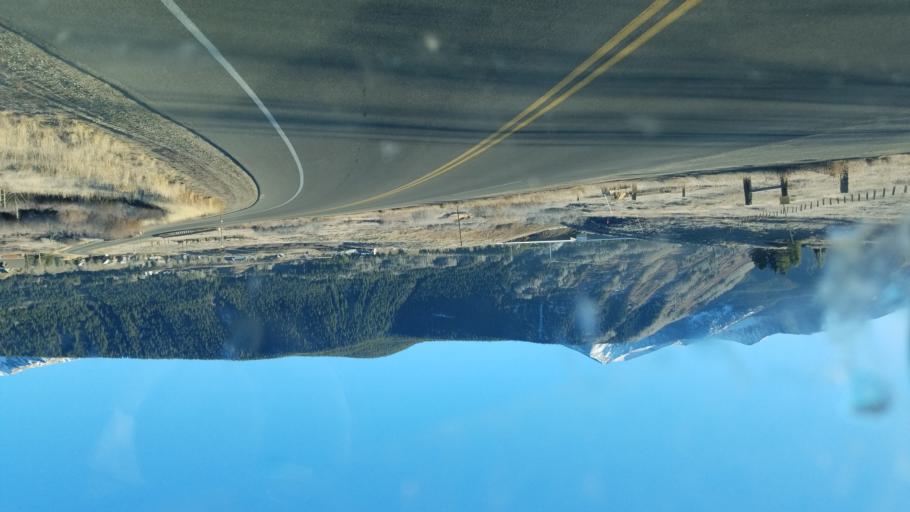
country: US
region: Colorado
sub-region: Gunnison County
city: Crested Butte
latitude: 38.8783
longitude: -106.9760
